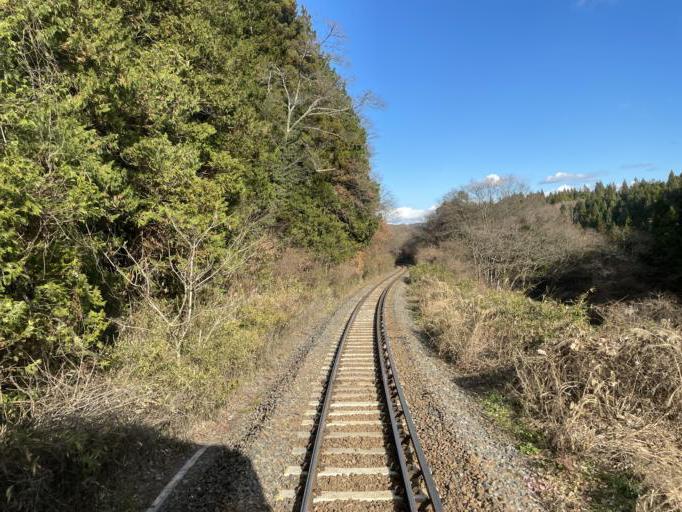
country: JP
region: Iwate
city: Ichinoseki
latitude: 38.9072
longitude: 141.2163
